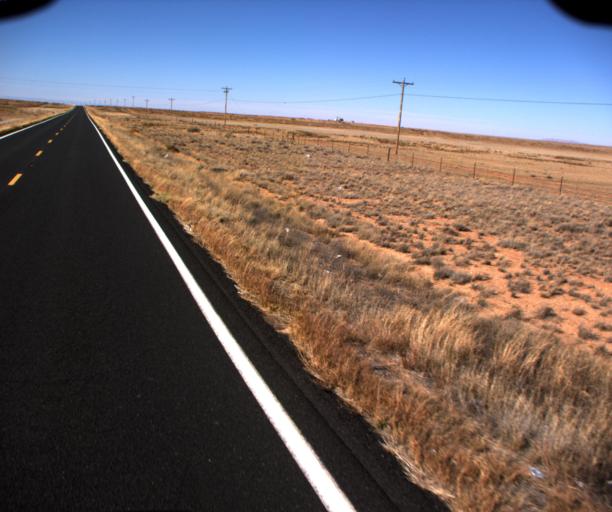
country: US
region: Arizona
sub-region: Coconino County
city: Tuba City
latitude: 36.0009
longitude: -111.0376
